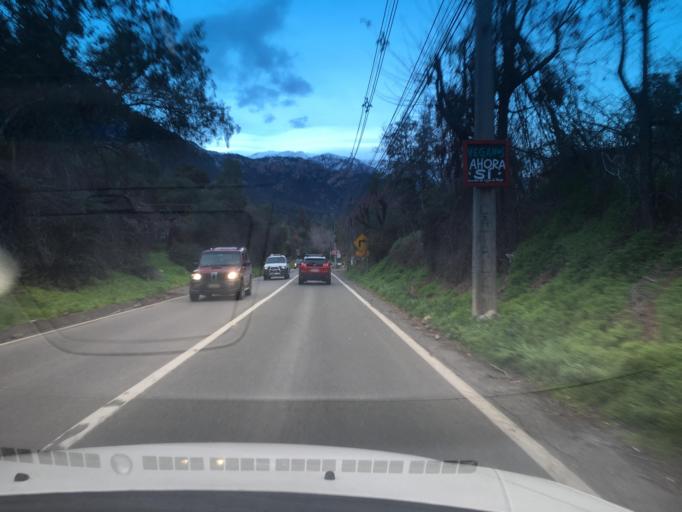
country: CL
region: Santiago Metropolitan
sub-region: Provincia de Cordillera
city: Puente Alto
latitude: -33.5795
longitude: -70.4113
